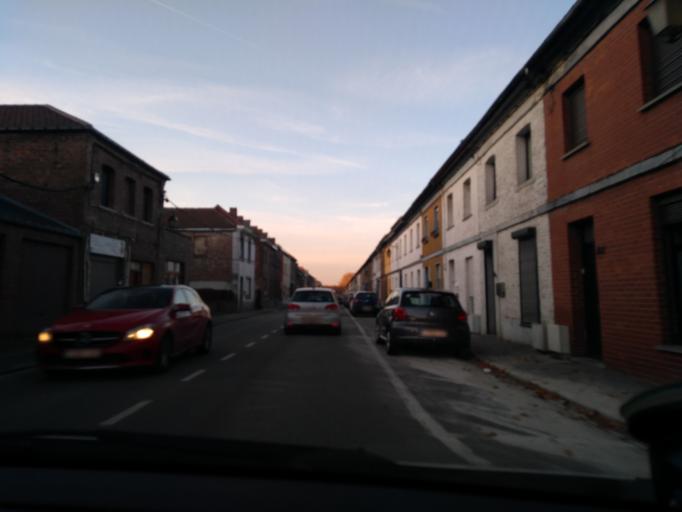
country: BE
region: Wallonia
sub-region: Province du Hainaut
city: Saint-Ghislain
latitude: 50.4350
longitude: 3.8363
